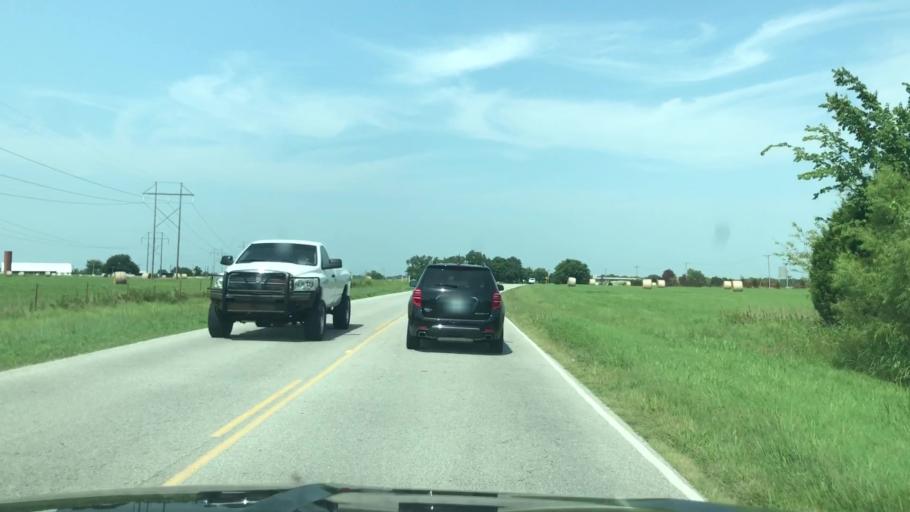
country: US
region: Oklahoma
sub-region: Ottawa County
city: Miami
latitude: 36.8797
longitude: -94.8452
